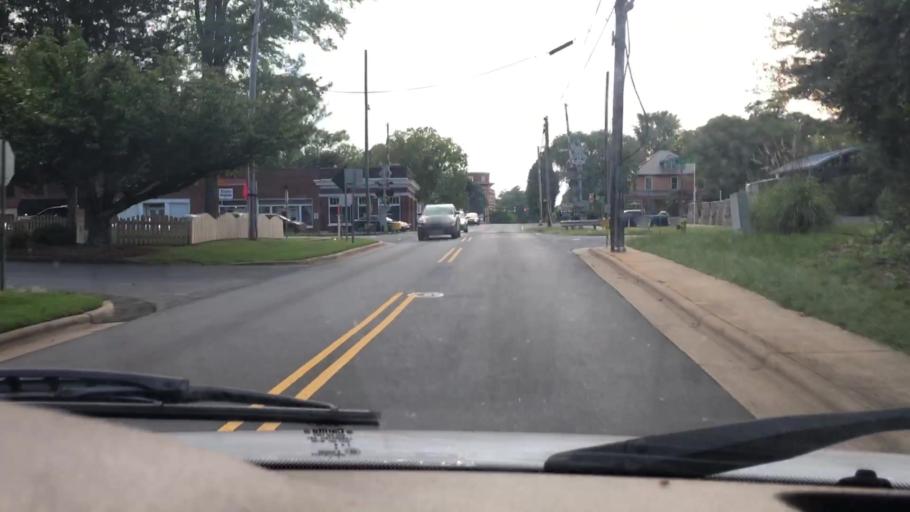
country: US
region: North Carolina
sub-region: Mecklenburg County
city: Huntersville
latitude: 35.4110
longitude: -80.8403
